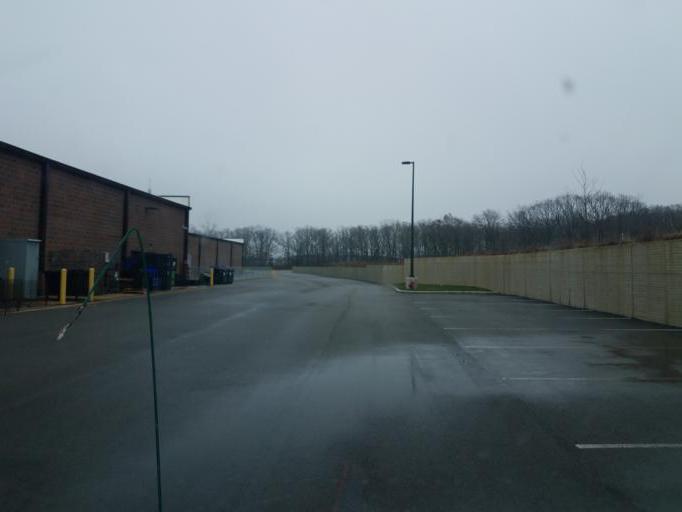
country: US
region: Ohio
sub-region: Union County
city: Marysville
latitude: 40.2401
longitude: -83.3967
